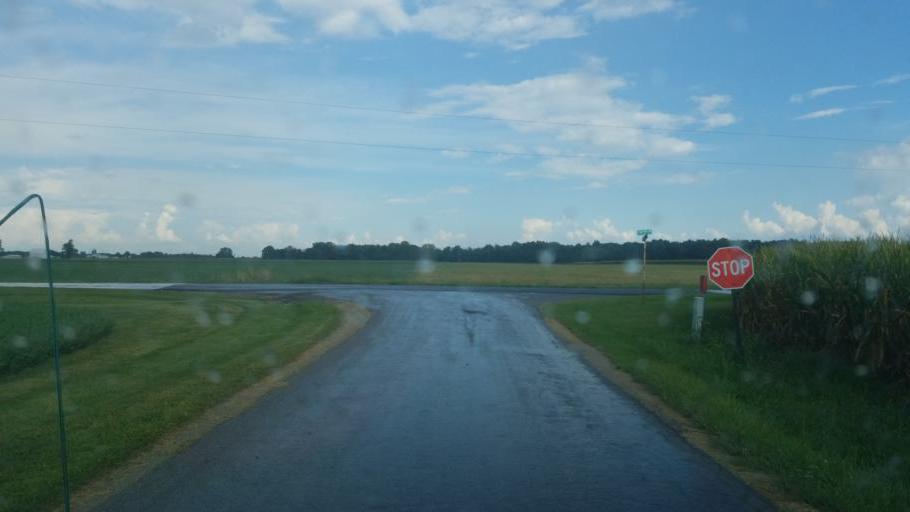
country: US
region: Ohio
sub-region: Huron County
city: Greenwich
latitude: 41.0093
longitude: -82.5595
